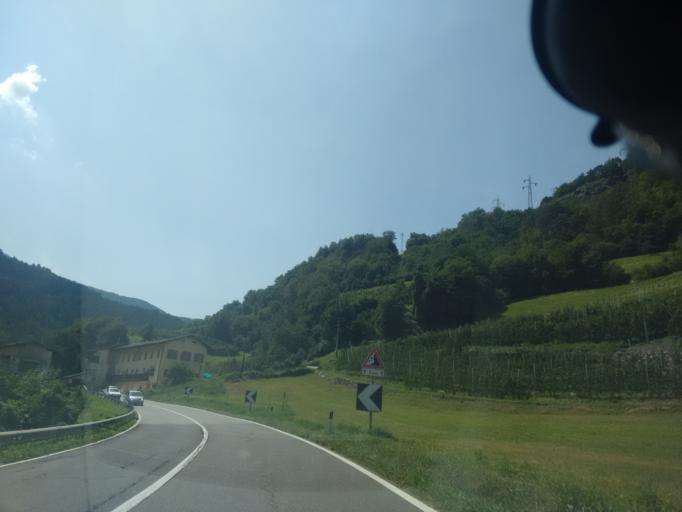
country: IT
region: Trentino-Alto Adige
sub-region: Bolzano
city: Velturno
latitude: 46.6631
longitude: 11.6079
